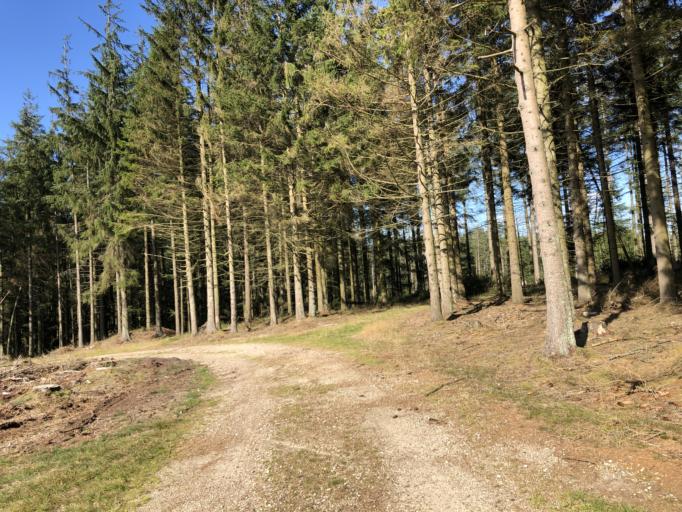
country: DK
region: Central Jutland
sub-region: Holstebro Kommune
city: Holstebro
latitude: 56.2488
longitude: 8.5006
